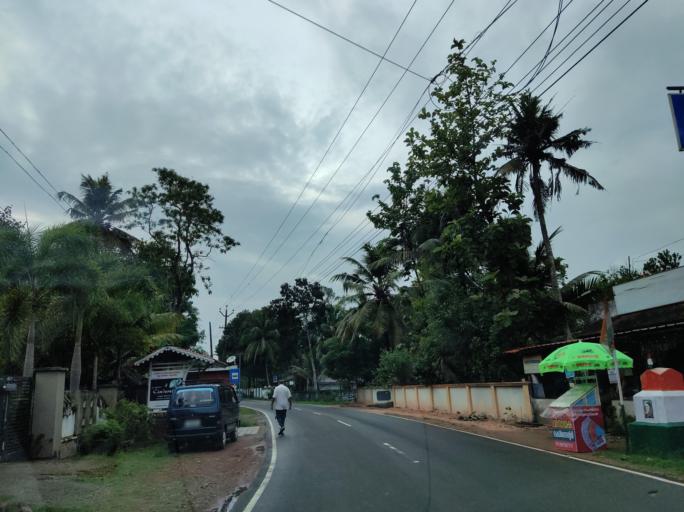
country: IN
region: Kerala
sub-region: Alappuzha
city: Mavelikara
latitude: 9.2300
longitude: 76.5714
